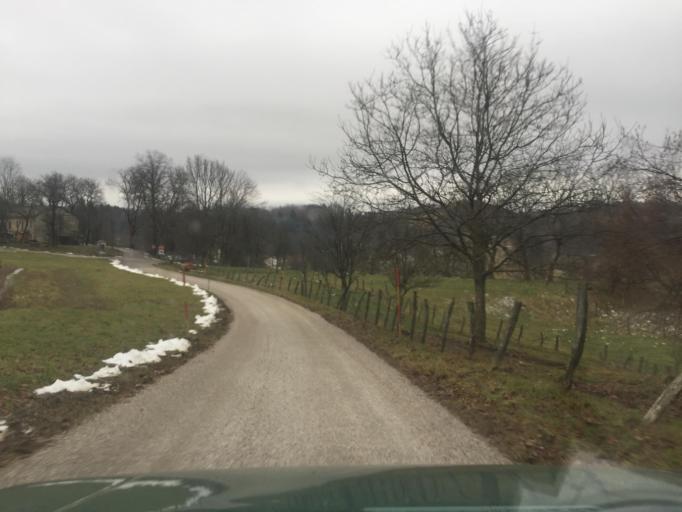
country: SI
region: Kanal
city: Kanal
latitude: 46.0663
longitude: 13.6988
